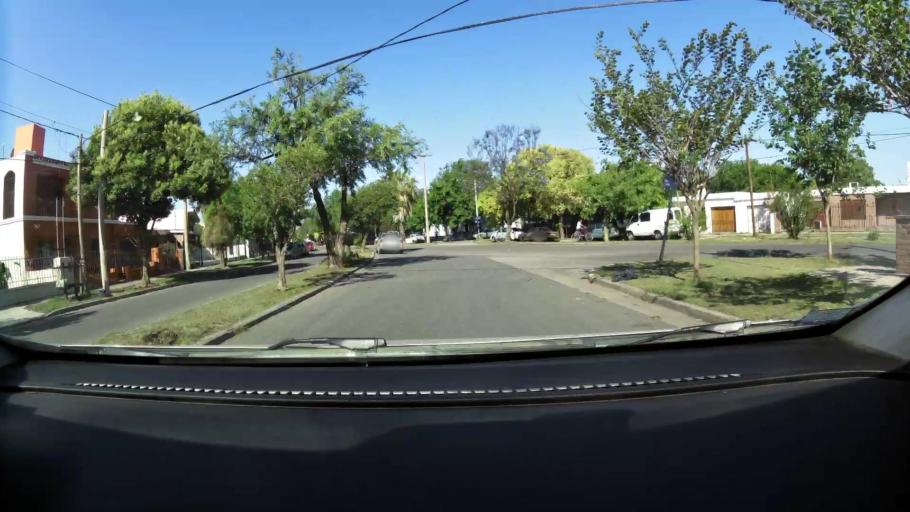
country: AR
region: Cordoba
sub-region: Departamento de Capital
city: Cordoba
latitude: -31.3626
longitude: -64.1964
